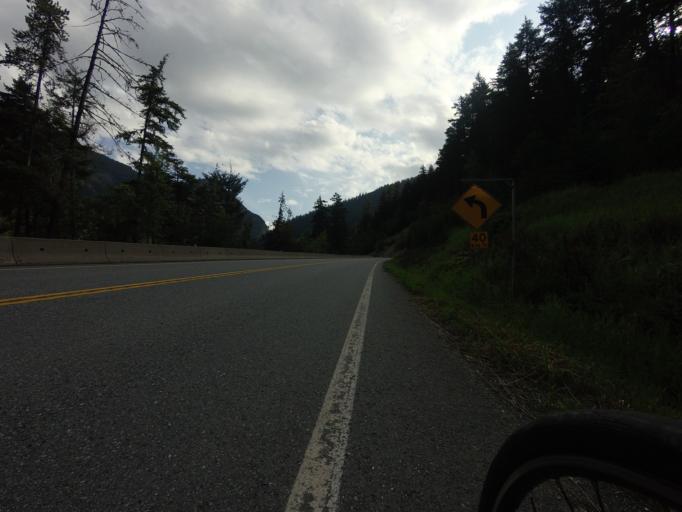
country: CA
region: British Columbia
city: Lillooet
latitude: 50.6295
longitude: -122.0926
